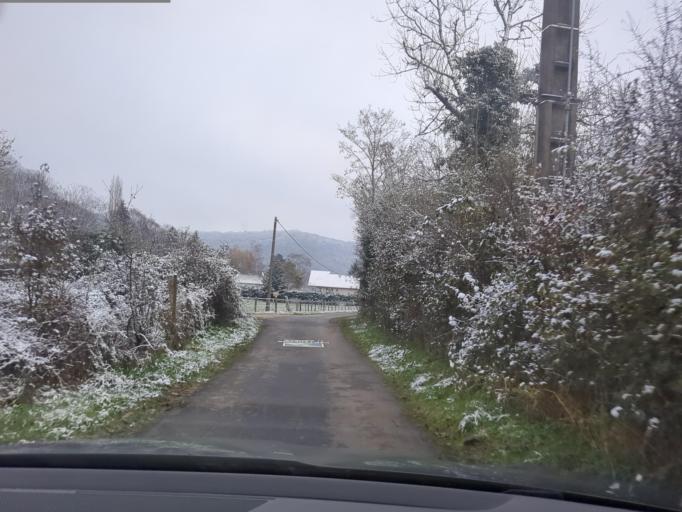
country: FR
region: Franche-Comte
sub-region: Departement du Jura
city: Perrigny
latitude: 46.6620
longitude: 5.5844
